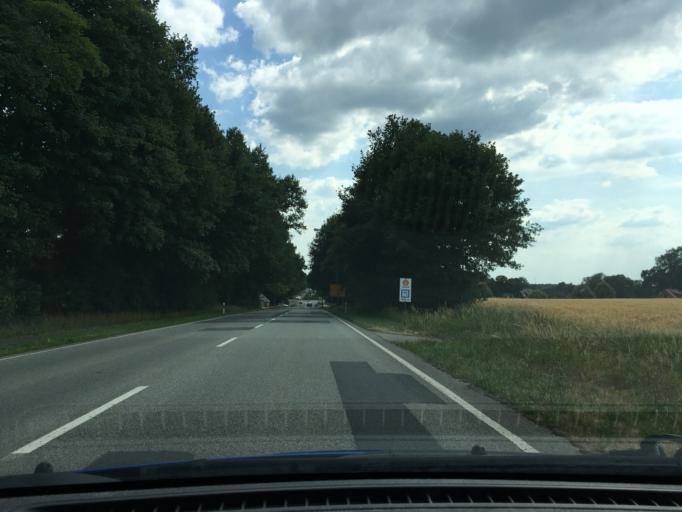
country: DE
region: Lower Saxony
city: Kakenstorf
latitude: 53.3125
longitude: 9.8045
